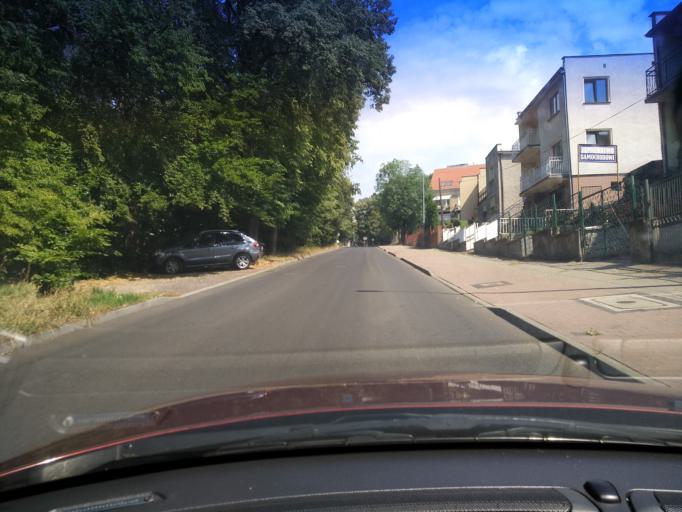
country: PL
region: Lower Silesian Voivodeship
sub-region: Powiat zgorzelecki
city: Zgorzelec
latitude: 51.1376
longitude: 15.0062
